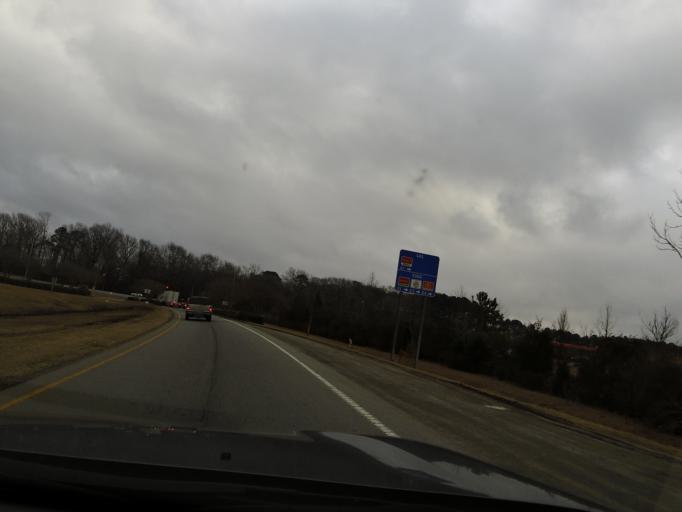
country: US
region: North Carolina
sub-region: Pitt County
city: Greenville
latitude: 35.6584
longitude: -77.3661
